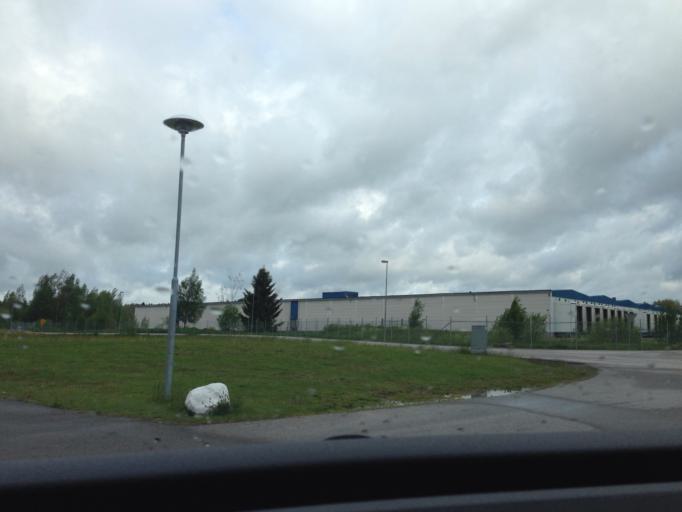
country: SE
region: Vaestra Goetaland
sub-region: Tibro Kommun
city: Tibro
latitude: 58.4178
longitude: 14.1323
